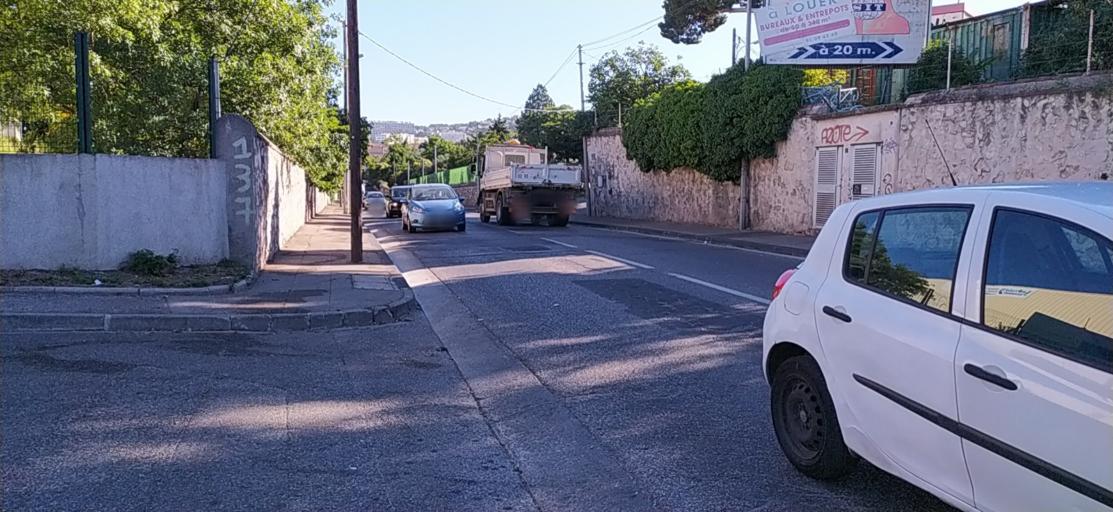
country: FR
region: Provence-Alpes-Cote d'Azur
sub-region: Departement des Bouches-du-Rhone
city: Marseille 14
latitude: 43.3424
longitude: 5.3654
